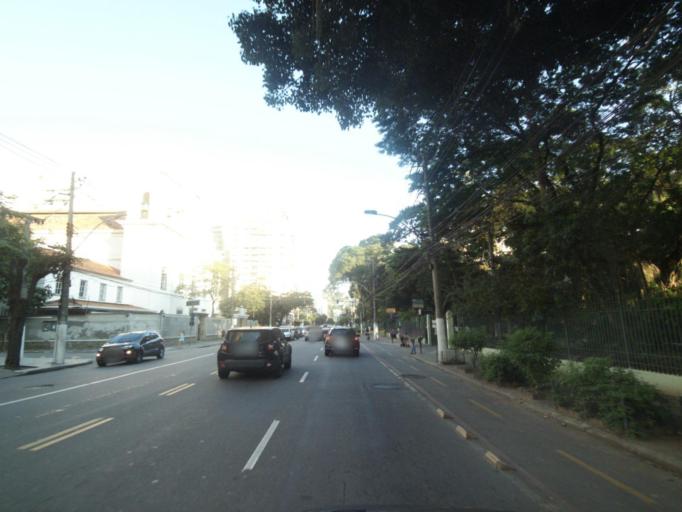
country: BR
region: Rio de Janeiro
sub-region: Niteroi
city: Niteroi
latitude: -22.9033
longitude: -43.1067
